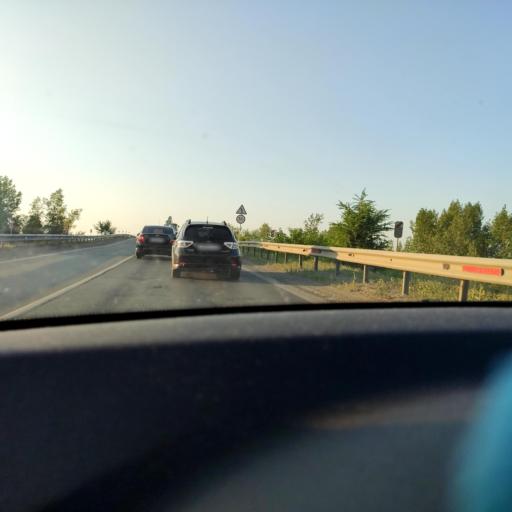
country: RU
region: Samara
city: Kinel'
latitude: 53.2498
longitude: 50.5913
